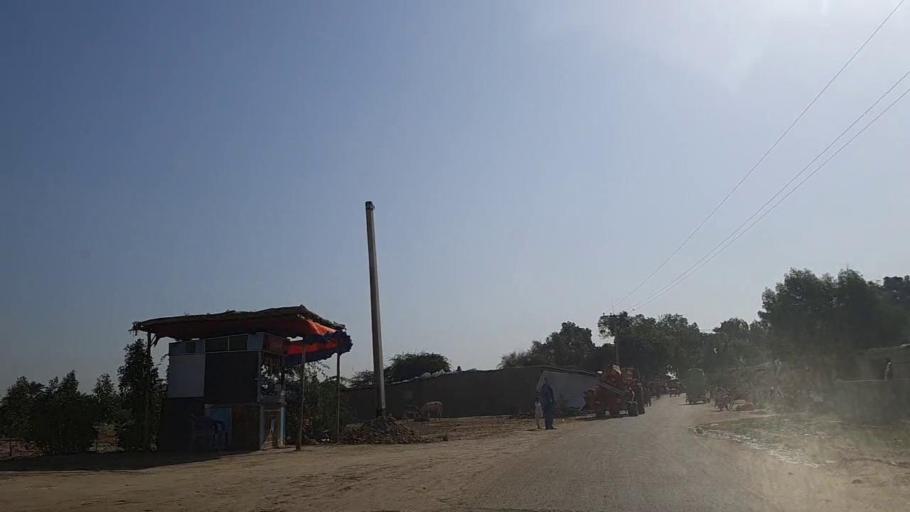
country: PK
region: Sindh
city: Jati
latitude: 24.5151
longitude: 68.2751
